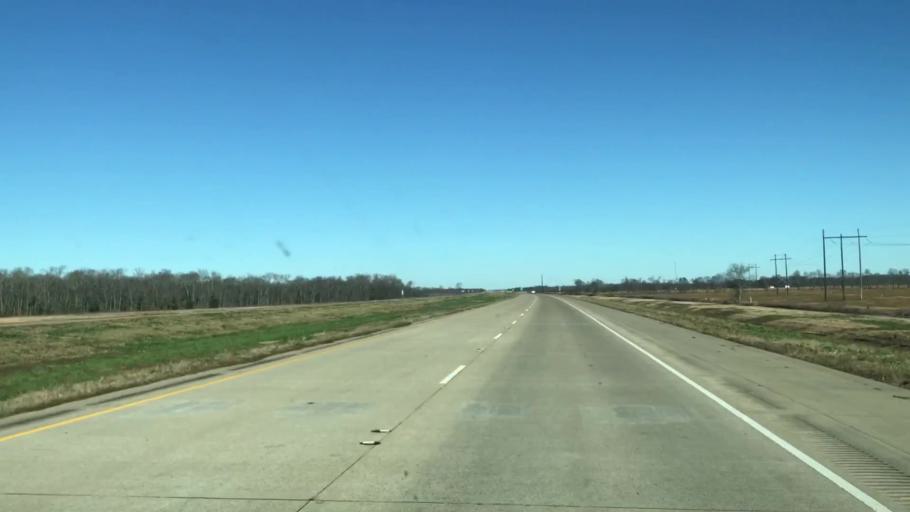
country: US
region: Louisiana
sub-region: Caddo Parish
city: Blanchard
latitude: 32.6546
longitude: -93.8419
